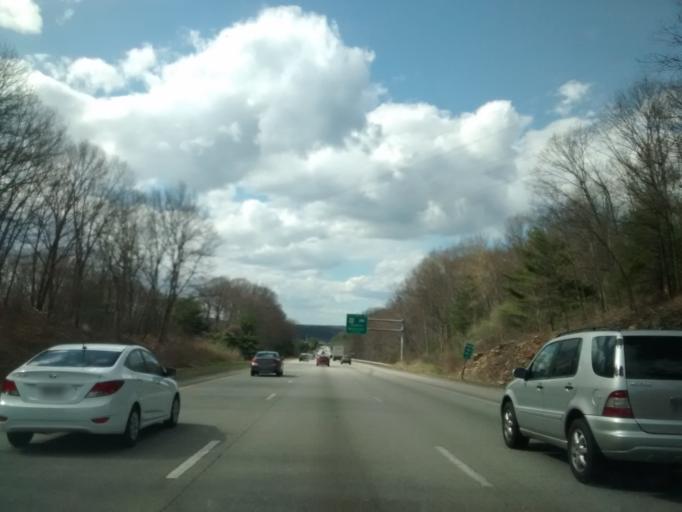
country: US
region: Massachusetts
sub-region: Middlesex County
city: Marlborough
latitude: 42.3524
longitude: -71.5785
